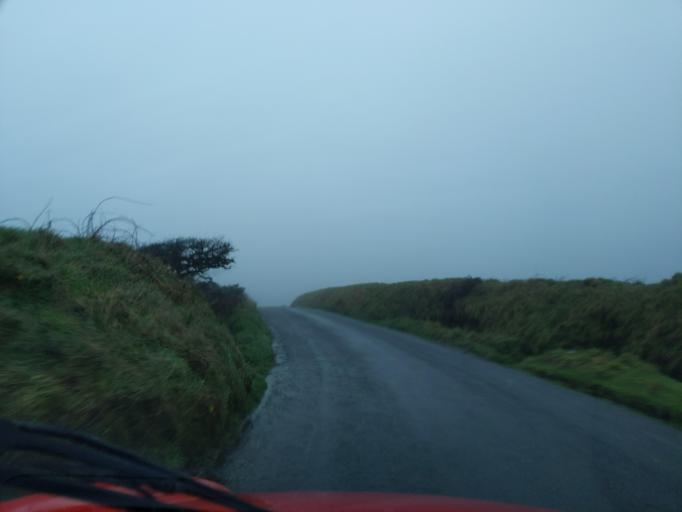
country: GB
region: England
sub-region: Cornwall
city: Camelford
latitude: 50.6534
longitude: -4.7016
